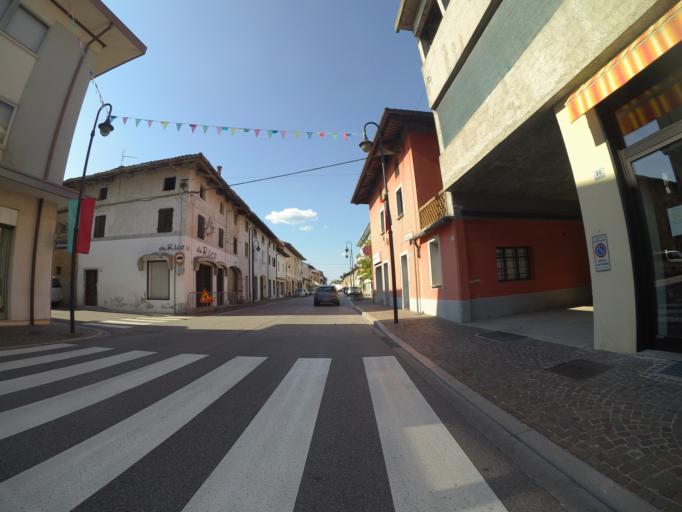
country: IT
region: Friuli Venezia Giulia
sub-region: Provincia di Udine
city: Mortegliano
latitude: 45.9454
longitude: 13.1724
